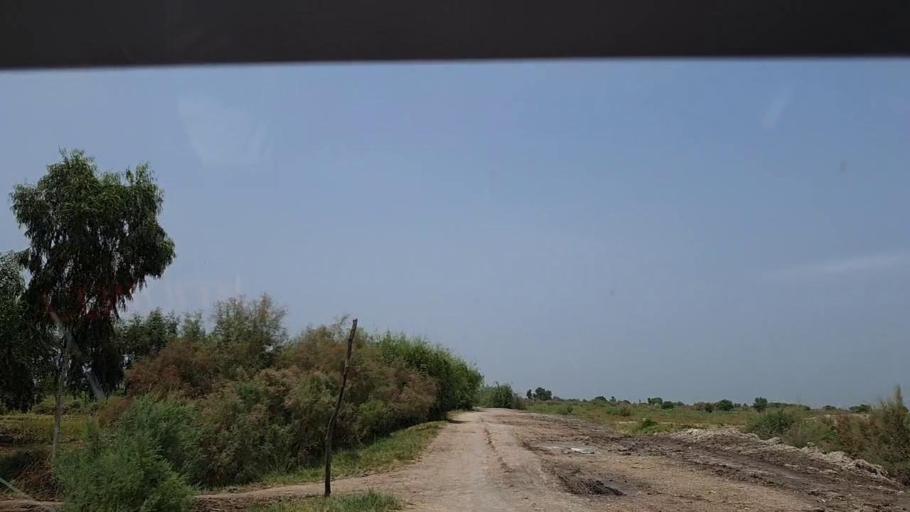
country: PK
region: Sindh
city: Adilpur
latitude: 27.8918
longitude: 69.2486
